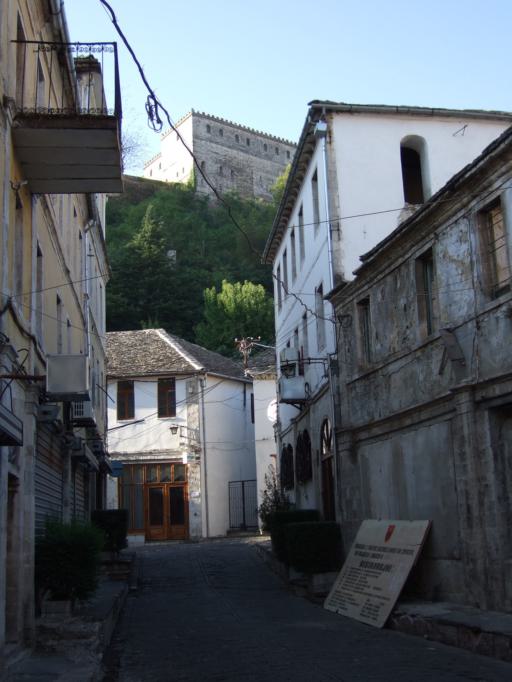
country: AL
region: Gjirokaster
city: Gjirokaster
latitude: 40.0748
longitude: 20.1389
